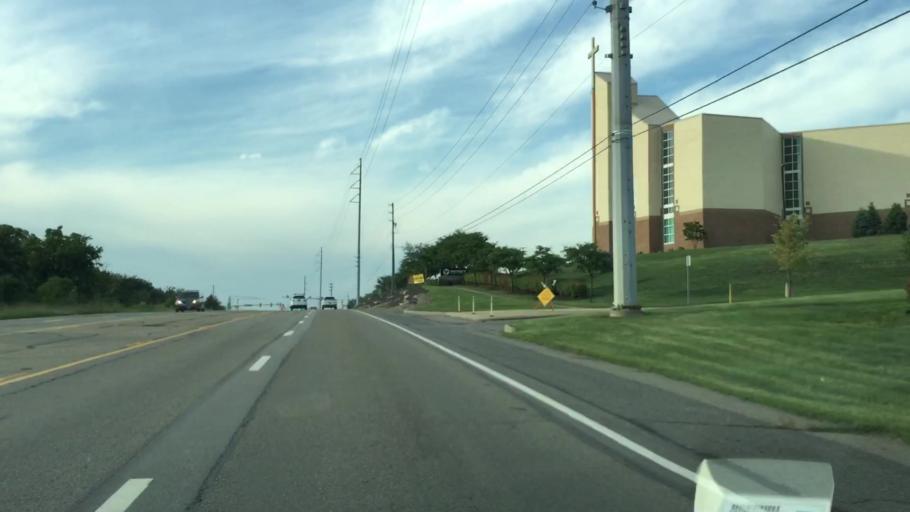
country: US
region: Pennsylvania
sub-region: Butler County
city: Fox Run
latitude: 40.7374
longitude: -80.1106
